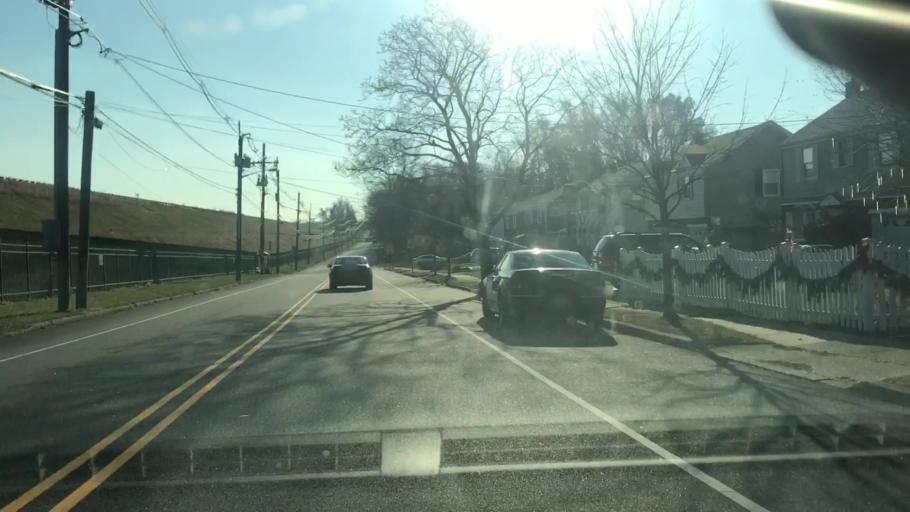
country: US
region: New Jersey
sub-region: Passaic County
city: Little Falls
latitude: 40.8638
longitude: -74.2135
